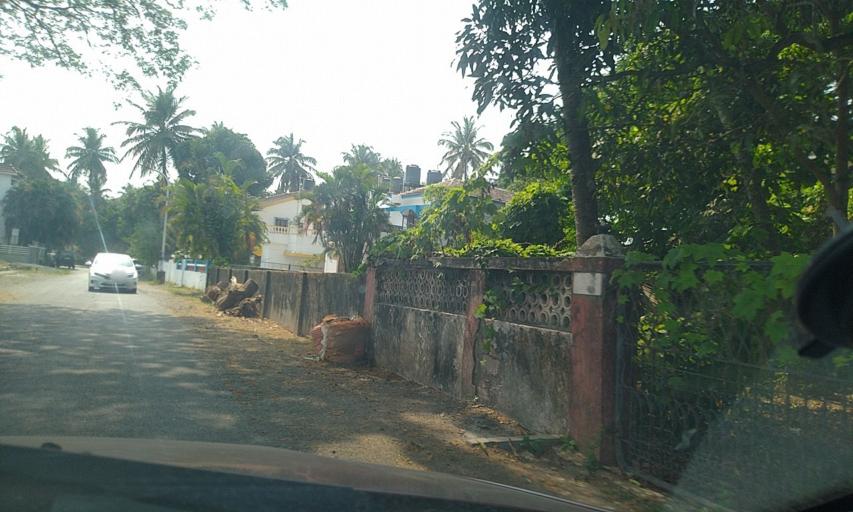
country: IN
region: Goa
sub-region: North Goa
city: Panaji
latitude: 15.4872
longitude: 73.8156
